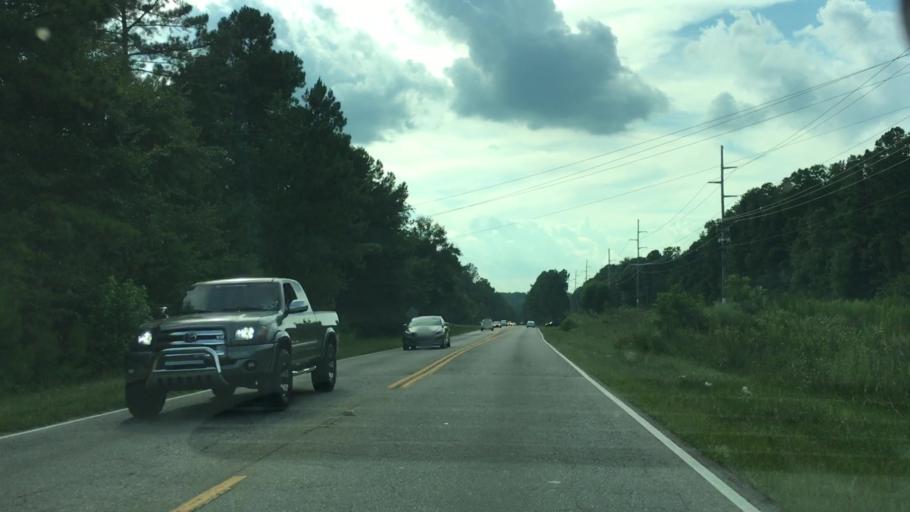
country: US
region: South Carolina
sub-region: Aiken County
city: Aiken
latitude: 33.5240
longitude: -81.7322
